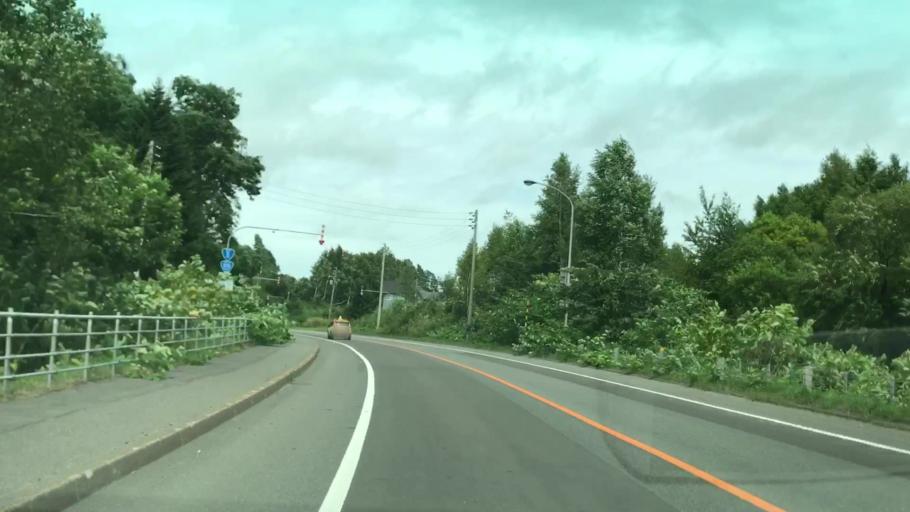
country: JP
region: Hokkaido
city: Niseko Town
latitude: 42.9113
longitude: 140.7533
